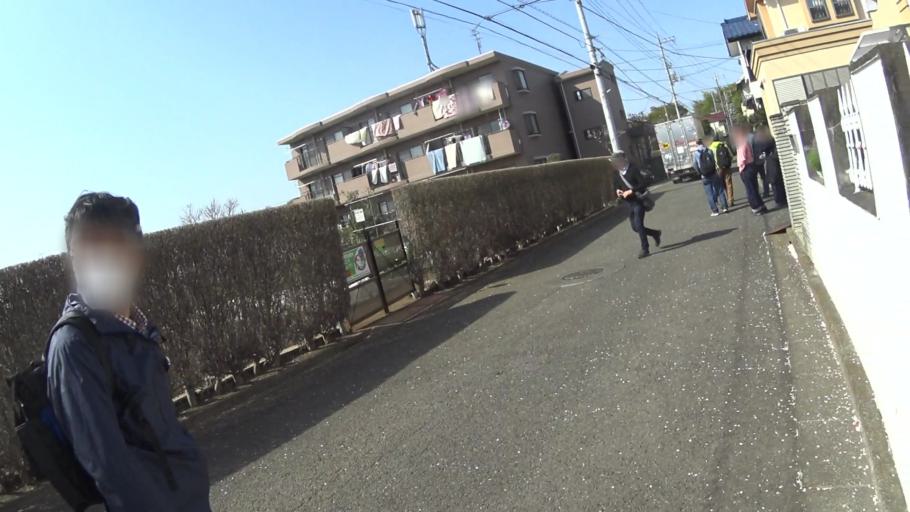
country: JP
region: Tokyo
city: Kokubunji
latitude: 35.7133
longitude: 139.4908
